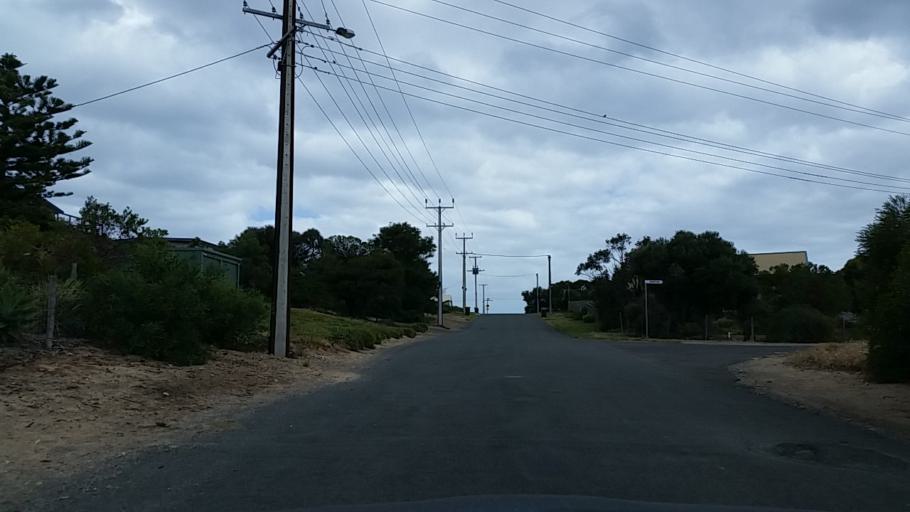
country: AU
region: South Australia
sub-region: Alexandrina
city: Port Elliot
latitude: -35.5336
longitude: 138.6691
